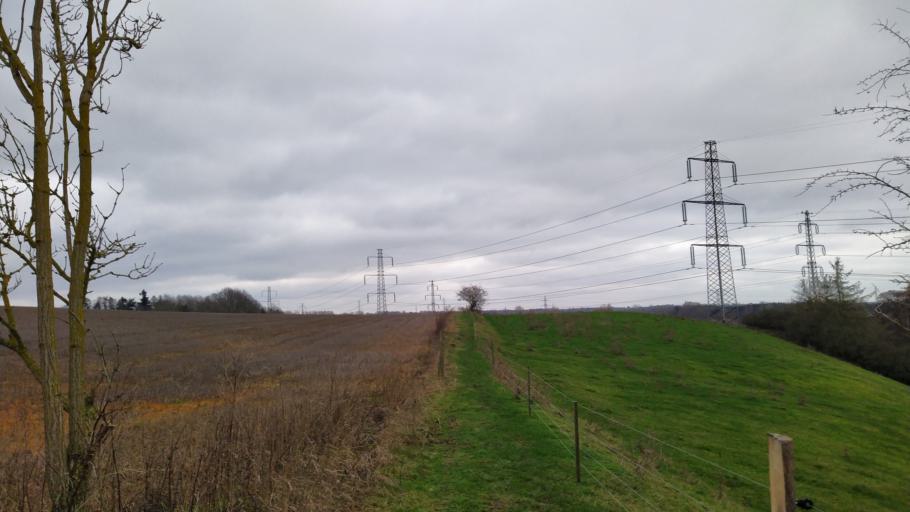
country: DK
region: Capital Region
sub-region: Egedal Kommune
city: Stenlose
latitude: 55.7552
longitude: 12.2149
